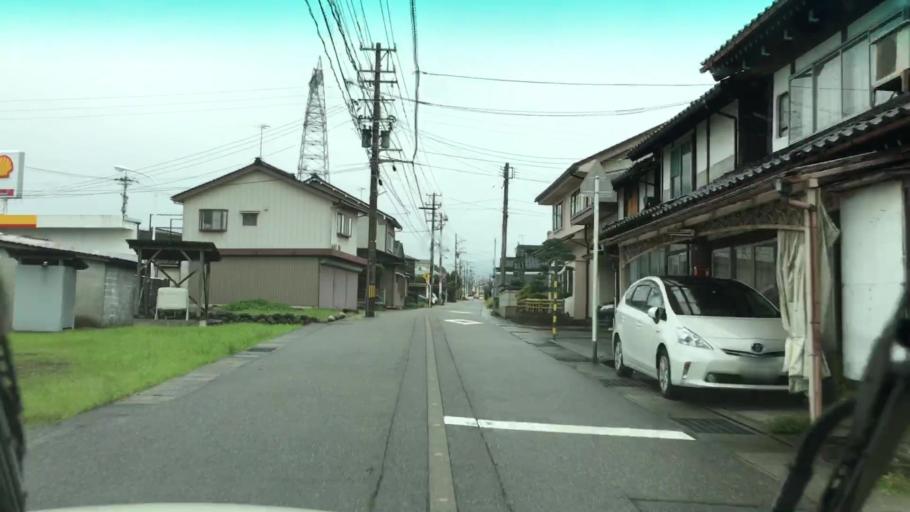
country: JP
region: Toyama
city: Kamiichi
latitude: 36.6533
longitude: 137.3189
